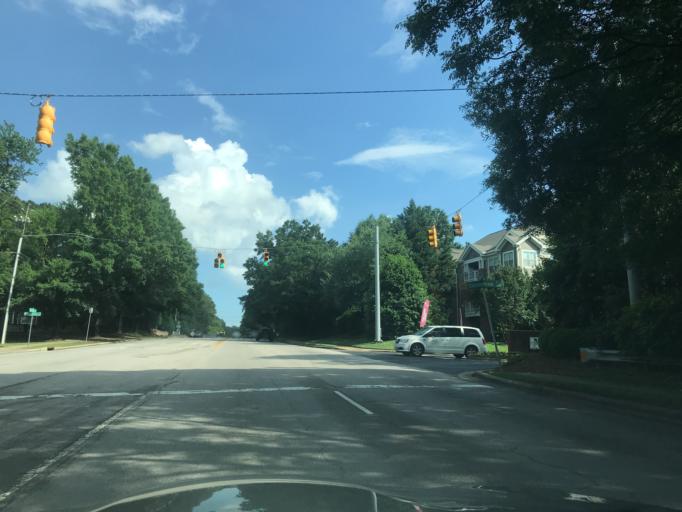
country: US
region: North Carolina
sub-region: Wake County
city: West Raleigh
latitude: 35.8742
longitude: -78.6440
